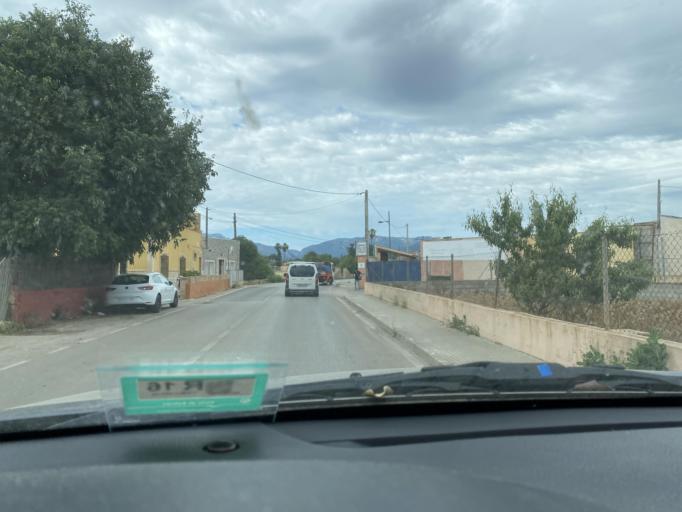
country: ES
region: Balearic Islands
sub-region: Illes Balears
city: Palma
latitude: 39.6088
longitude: 2.6797
